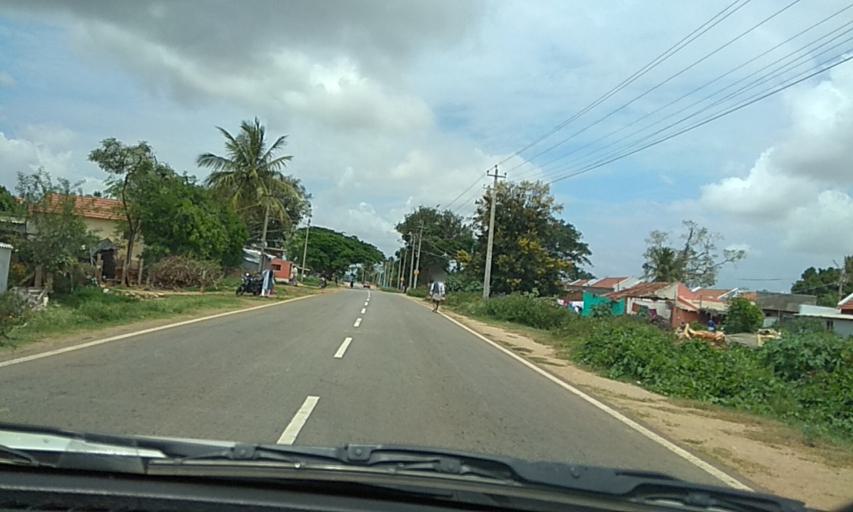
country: IN
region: Karnataka
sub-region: Chamrajnagar
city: Gundlupet
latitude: 11.8154
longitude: 76.7573
